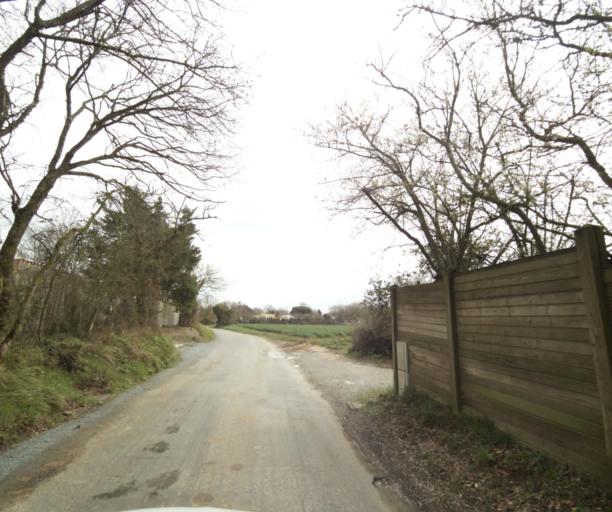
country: FR
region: Poitou-Charentes
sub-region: Departement de la Charente-Maritime
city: Lagord
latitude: 46.1896
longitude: -1.1697
